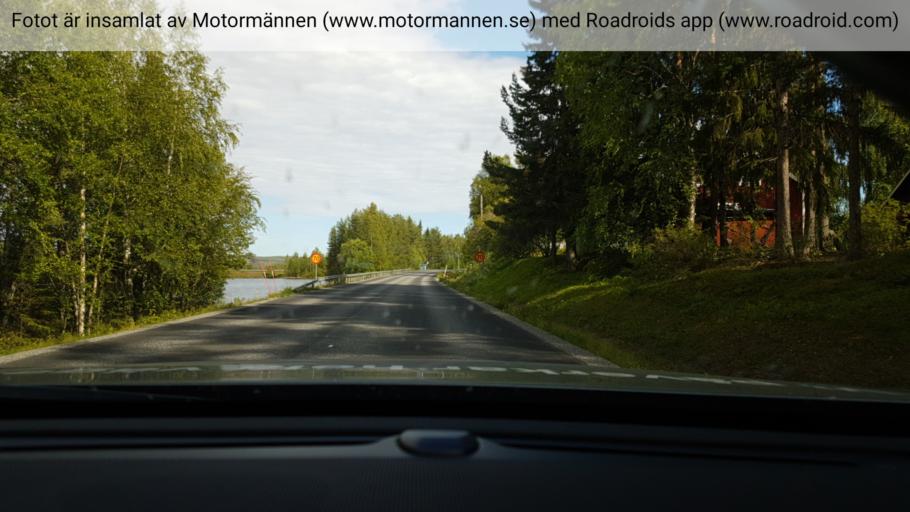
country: SE
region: Vaesterbotten
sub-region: Lycksele Kommun
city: Soderfors
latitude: 64.8285
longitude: 18.0426
